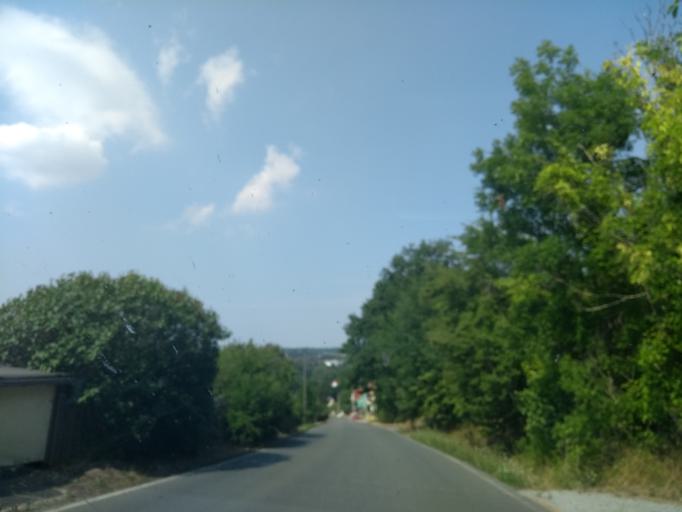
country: DE
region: Thuringia
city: Eisenberg
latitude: 50.9733
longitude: 11.9090
